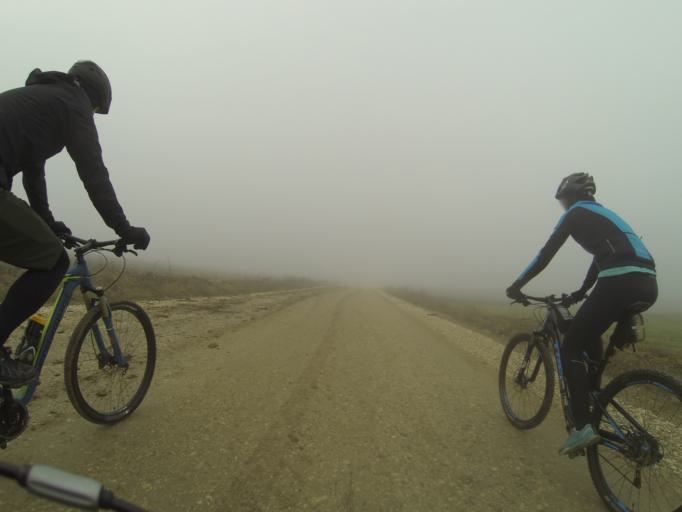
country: RO
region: Mehedinti
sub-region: Comuna Balacita
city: Gvardinita
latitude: 44.4181
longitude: 23.1333
